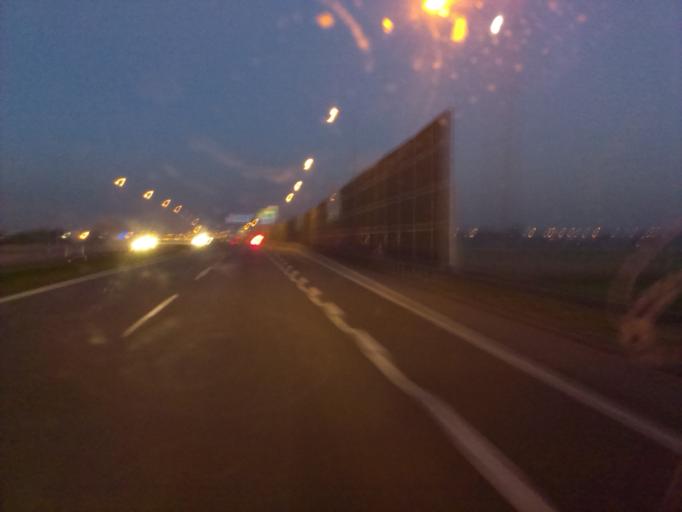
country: PL
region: Silesian Voivodeship
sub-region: Gliwice
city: Gliwice
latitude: 50.2589
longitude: 18.7011
